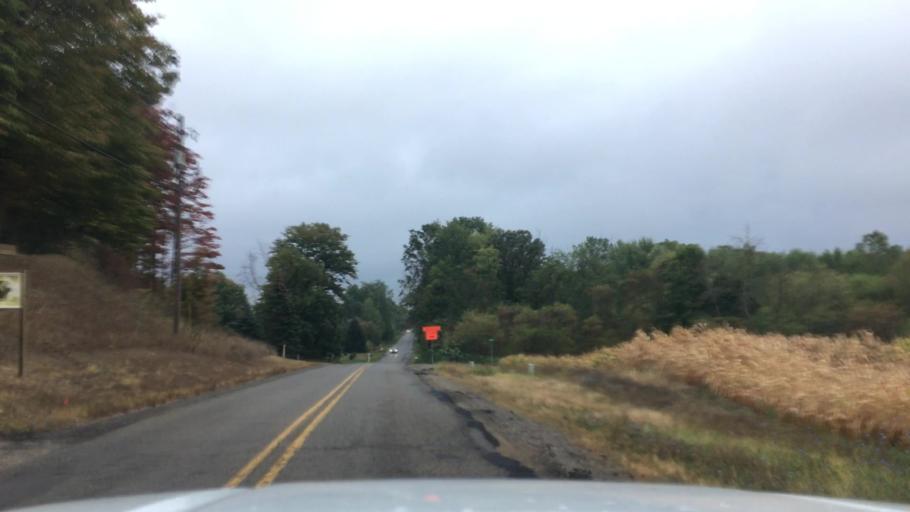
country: US
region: Michigan
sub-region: Ottawa County
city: Hudsonville
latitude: 42.8407
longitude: -85.8230
